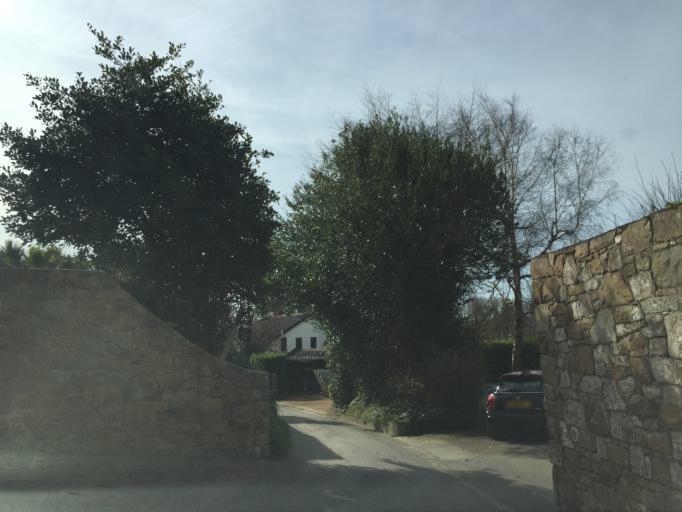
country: JE
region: St Helier
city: Saint Helier
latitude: 49.2213
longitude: -2.1491
